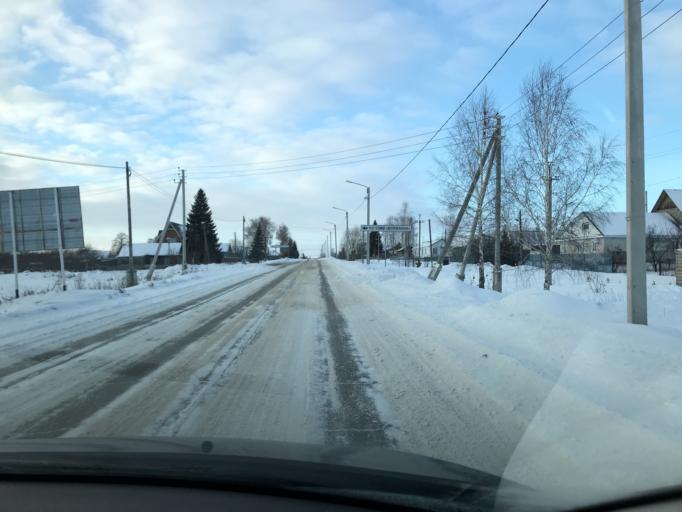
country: RU
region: Ulyanovsk
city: Undory
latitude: 54.6031
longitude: 48.4145
